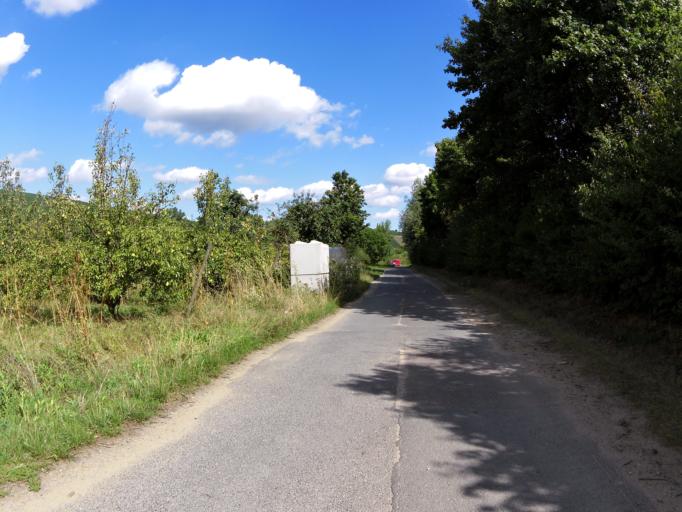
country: DE
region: Bavaria
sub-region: Regierungsbezirk Unterfranken
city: Nordheim
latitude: 49.8538
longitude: 10.1741
